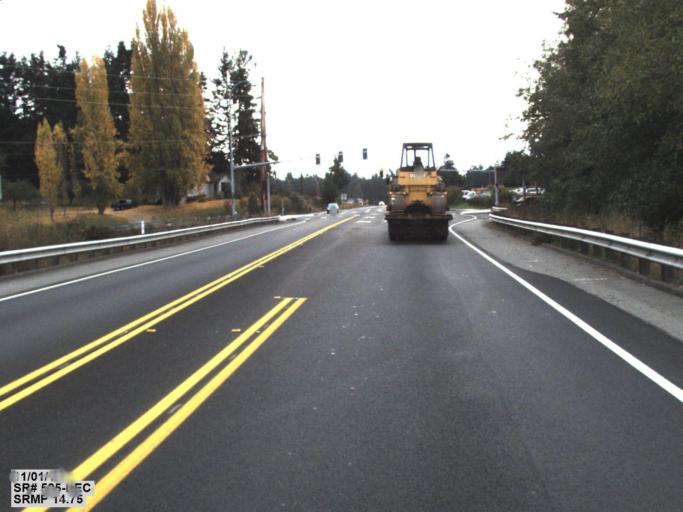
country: US
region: Washington
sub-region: Island County
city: Freeland
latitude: 48.0052
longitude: -122.4624
